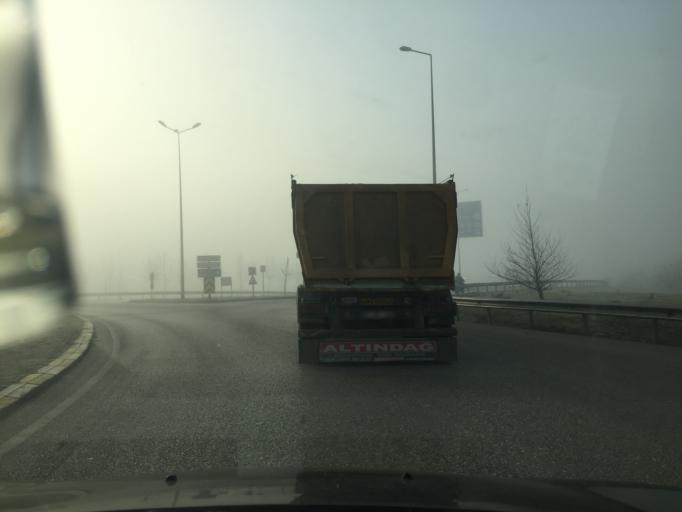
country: TR
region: Duzce
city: Duzce
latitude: 40.8643
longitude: 31.2147
